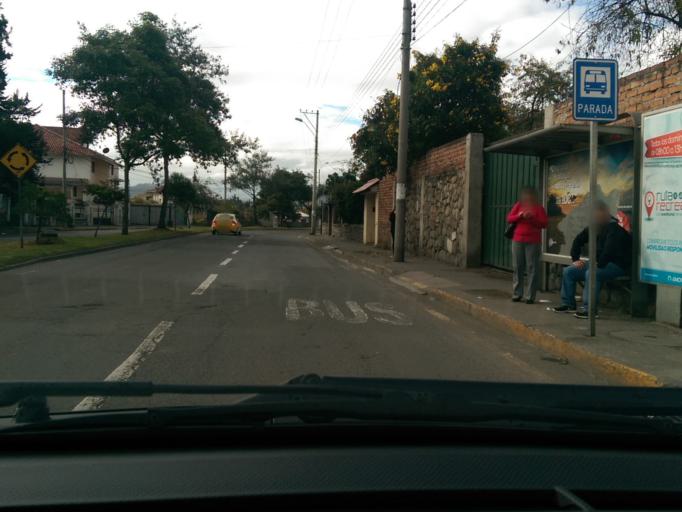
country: EC
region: Azuay
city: Cuenca
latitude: -2.8971
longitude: -79.0143
